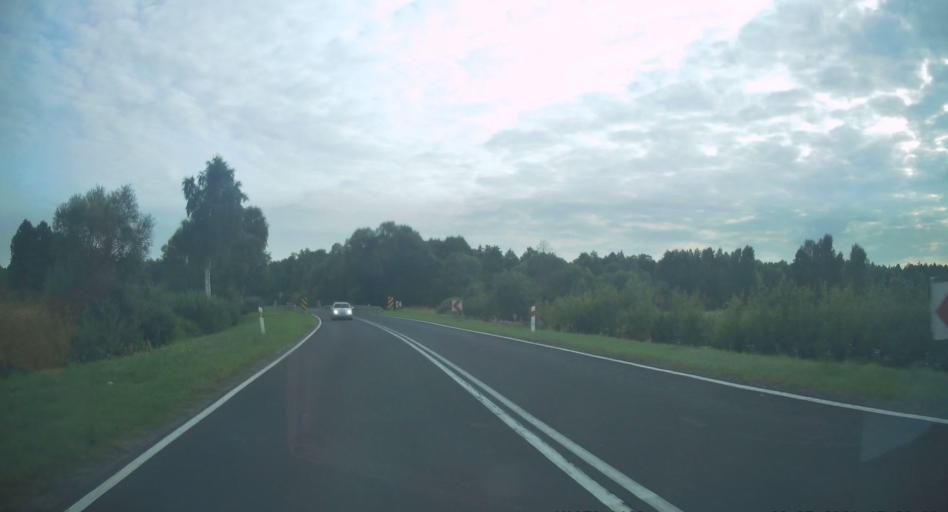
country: PL
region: Lodz Voivodeship
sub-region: Powiat radomszczanski
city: Plawno
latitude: 51.0159
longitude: 19.4230
